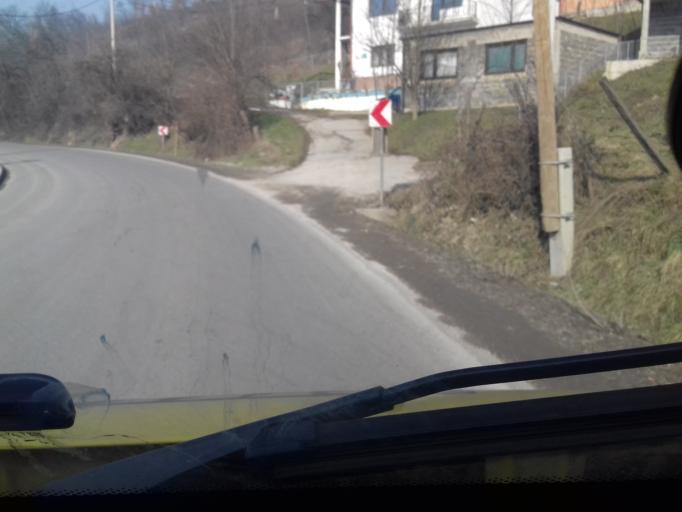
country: BA
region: Federation of Bosnia and Herzegovina
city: Ilijas
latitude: 43.9401
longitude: 18.2798
